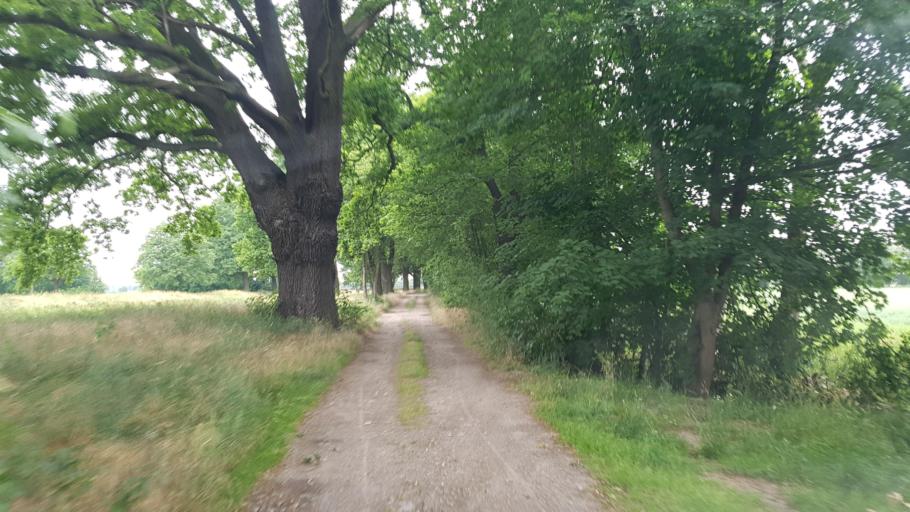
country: DE
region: Brandenburg
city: Grossthiemig
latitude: 51.4066
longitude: 13.6526
